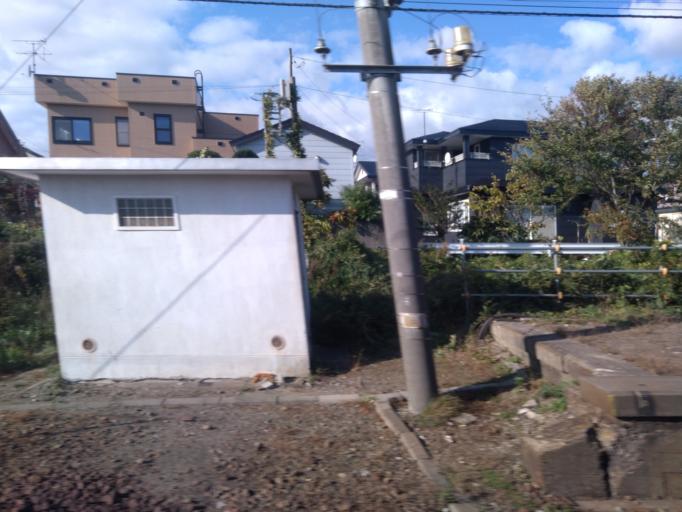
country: JP
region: Hokkaido
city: Muroran
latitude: 42.3592
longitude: 141.0416
